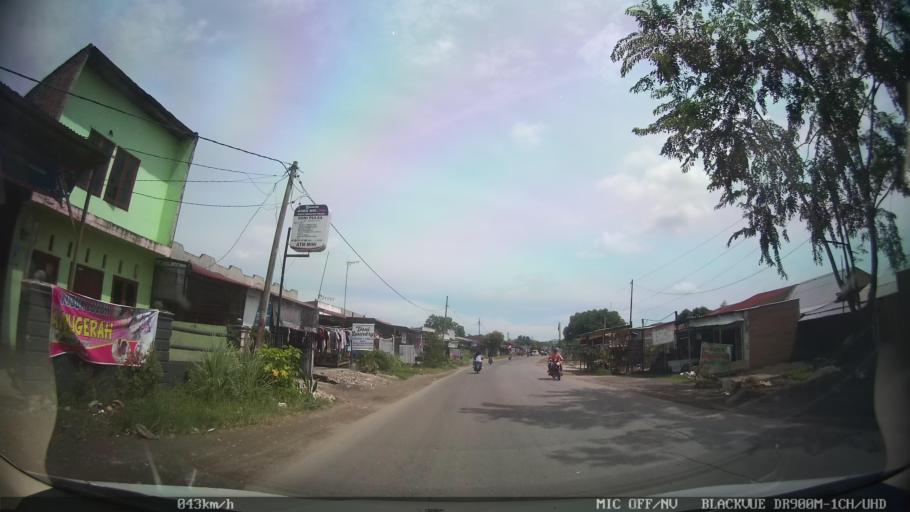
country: ID
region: North Sumatra
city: Medan
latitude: 3.6479
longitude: 98.7086
